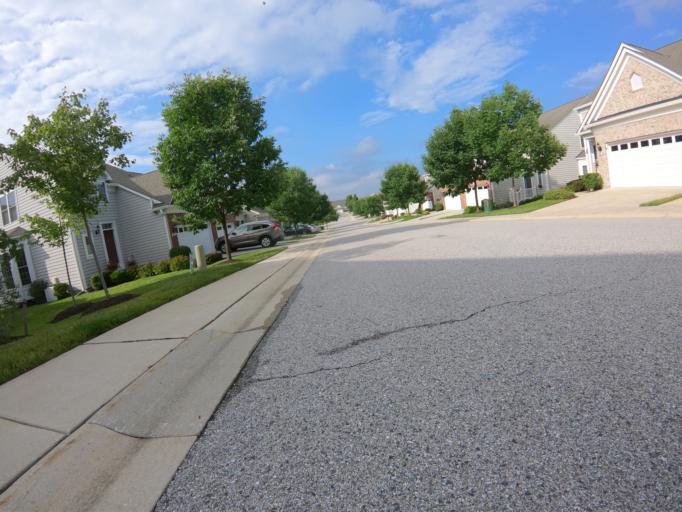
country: US
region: Maryland
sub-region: Howard County
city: Ellicott City
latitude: 39.2542
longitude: -76.7905
